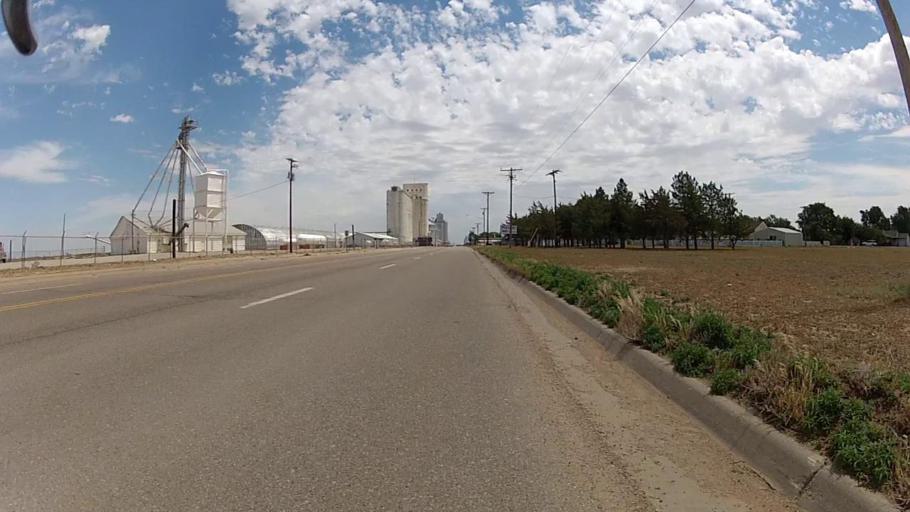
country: US
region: Kansas
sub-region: Haskell County
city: Satanta
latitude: 37.4375
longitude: -100.9948
